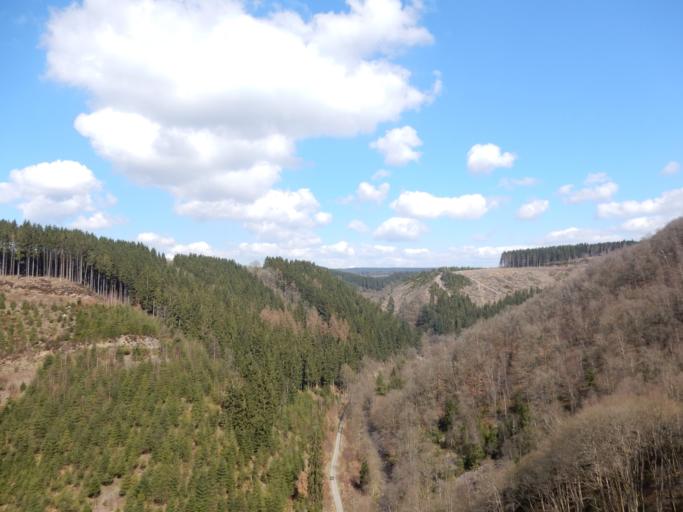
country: BE
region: Wallonia
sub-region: Province de Liege
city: Waimes
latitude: 50.4493
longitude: 6.0901
